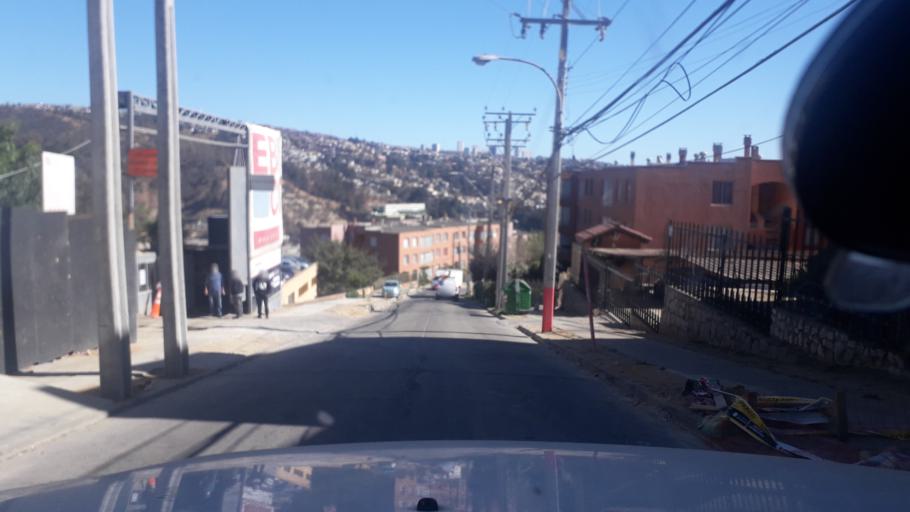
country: CL
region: Valparaiso
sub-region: Provincia de Valparaiso
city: Vina del Mar
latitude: -33.0376
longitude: -71.5145
